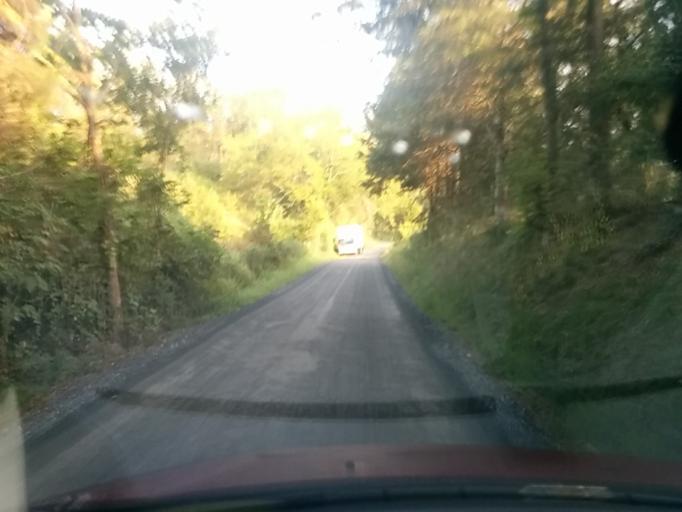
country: US
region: Virginia
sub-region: City of Lexington
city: Lexington
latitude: 37.7576
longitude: -79.4469
